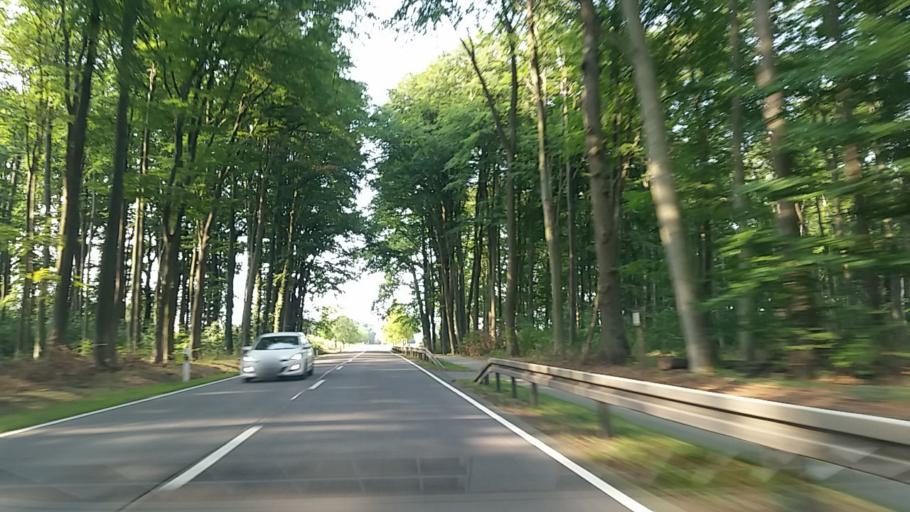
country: DE
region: Mecklenburg-Vorpommern
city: Hagenow
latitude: 53.4105
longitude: 11.1267
